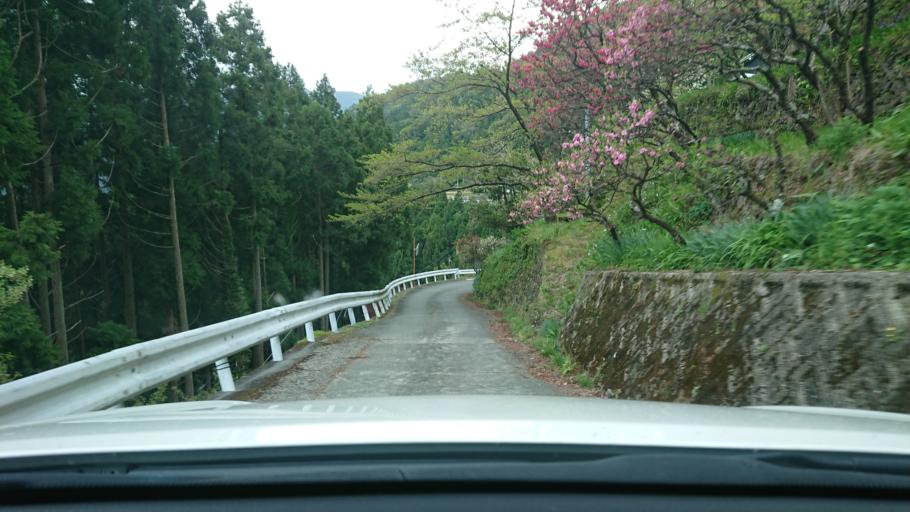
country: JP
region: Tokushima
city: Kamojimacho-jogejima
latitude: 33.8866
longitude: 134.3783
